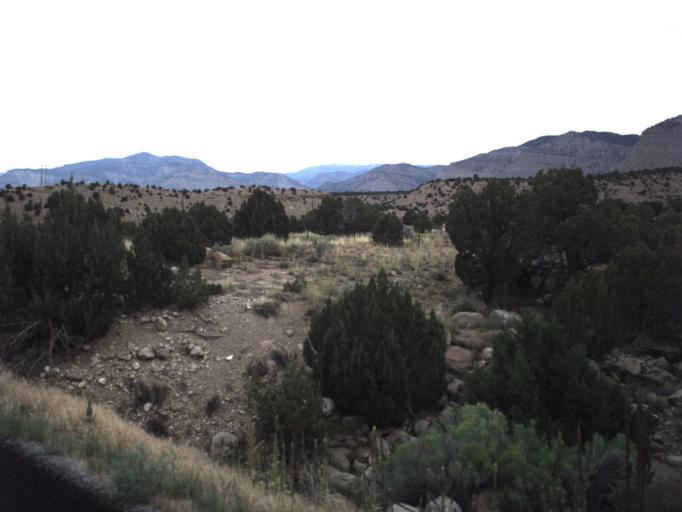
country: US
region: Utah
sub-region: Carbon County
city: East Carbon City
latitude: 39.4786
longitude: -110.3996
